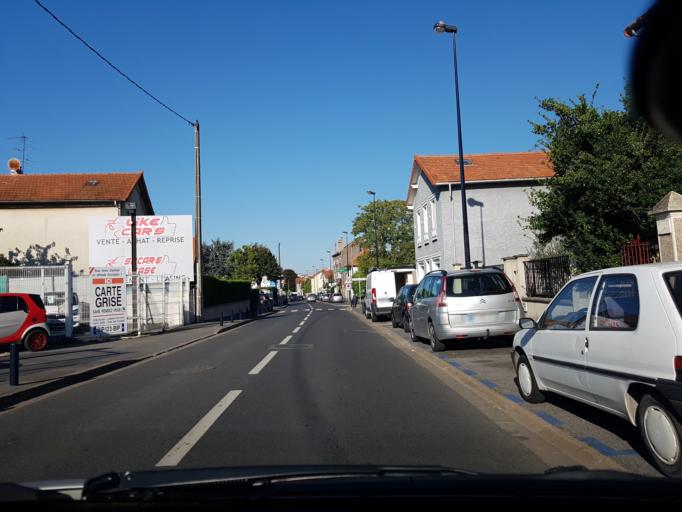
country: FR
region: Ile-de-France
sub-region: Departement du Val-de-Marne
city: Chennevieres-sur-Marne
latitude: 48.8152
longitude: 2.5382
